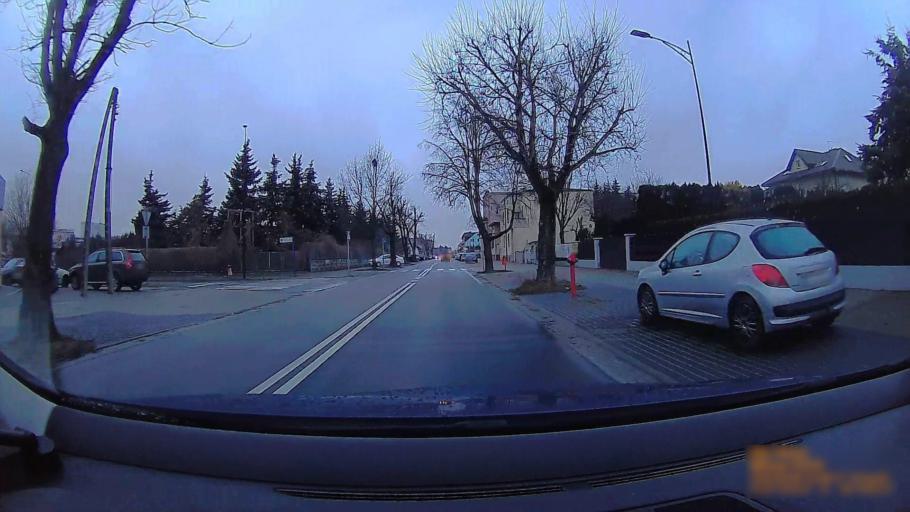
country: PL
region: Greater Poland Voivodeship
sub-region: Konin
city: Konin
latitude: 52.2066
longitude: 18.2587
